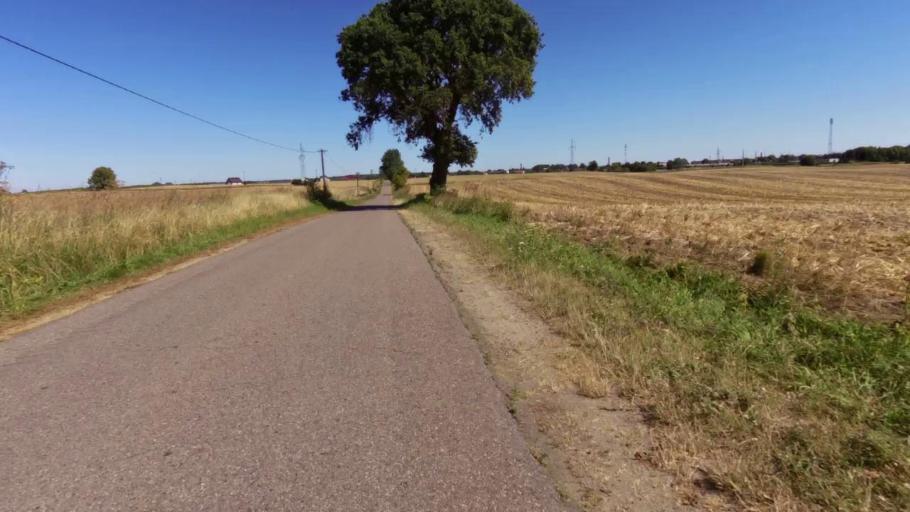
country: PL
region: West Pomeranian Voivodeship
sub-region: Powiat drawski
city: Czaplinek
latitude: 53.5478
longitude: 16.2148
